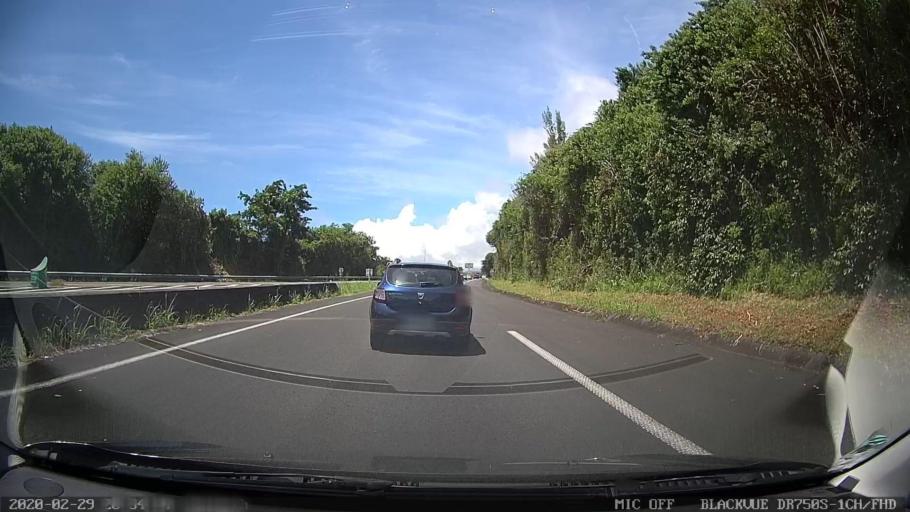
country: RE
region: Reunion
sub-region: Reunion
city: Saint-Benoit
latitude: -21.0294
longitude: 55.7046
